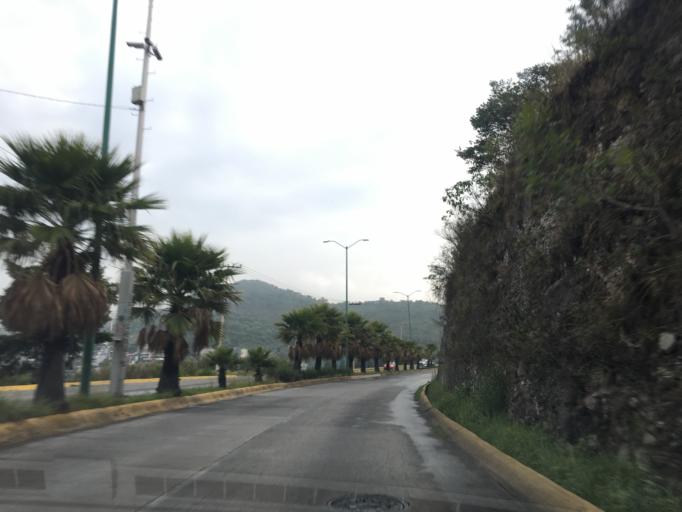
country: MX
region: Mexico
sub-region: Naucalpan de Juarez
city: Rincon Verde
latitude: 19.5261
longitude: -99.2654
